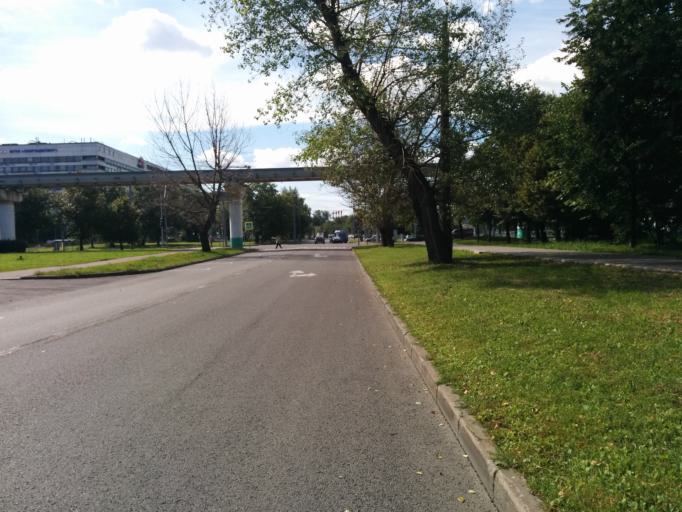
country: RU
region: Moscow
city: Ostankinskiy
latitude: 55.8224
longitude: 37.6167
